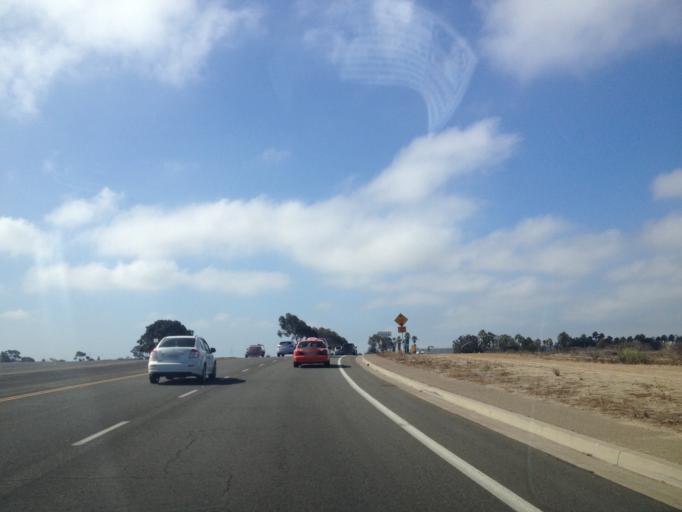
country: US
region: California
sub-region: San Diego County
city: San Diego
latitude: 32.7660
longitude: -117.2088
